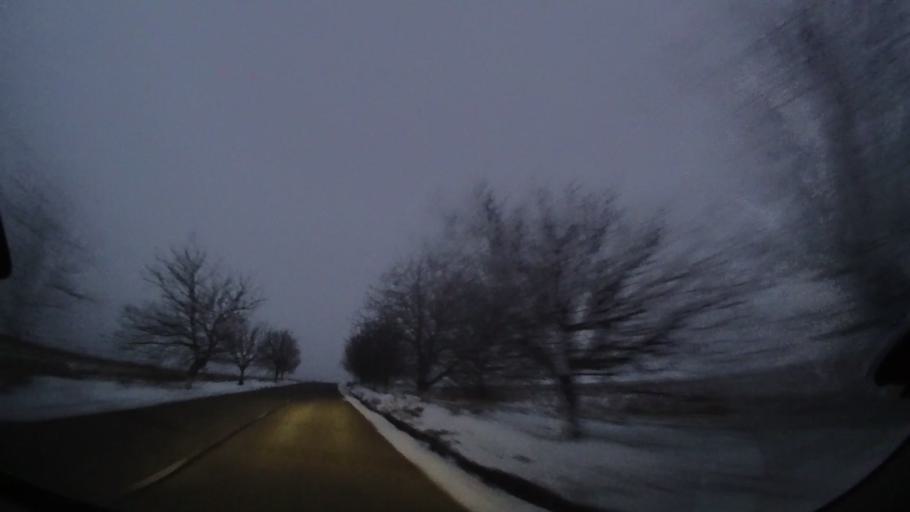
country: RO
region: Vaslui
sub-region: Comuna Hoceni
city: Hoceni
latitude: 46.5219
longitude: 28.0261
